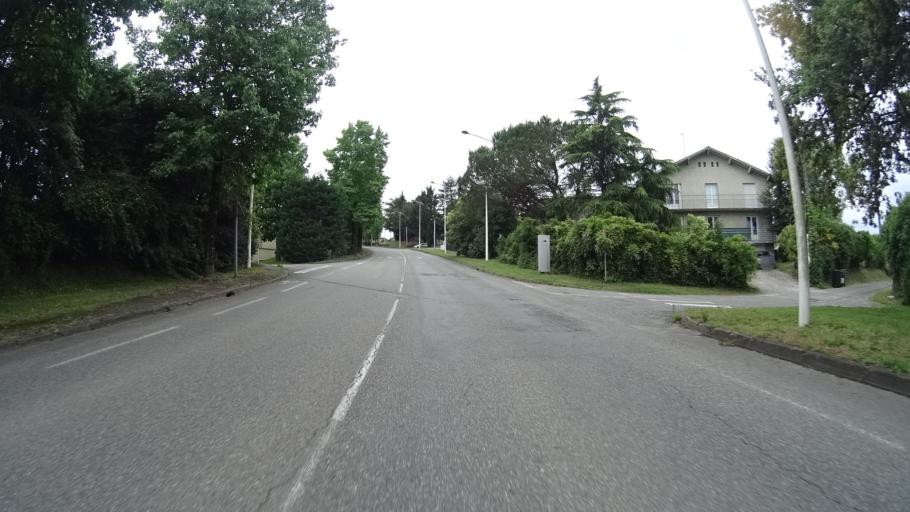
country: FR
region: Aquitaine
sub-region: Departement des Pyrenees-Atlantiques
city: Orthez
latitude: 43.4885
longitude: -0.7594
